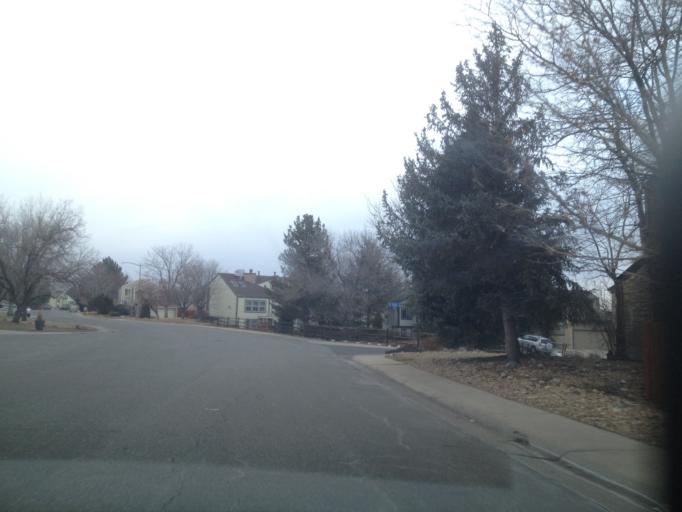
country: US
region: Colorado
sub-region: Adams County
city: Westminster
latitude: 39.8169
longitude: -105.0461
